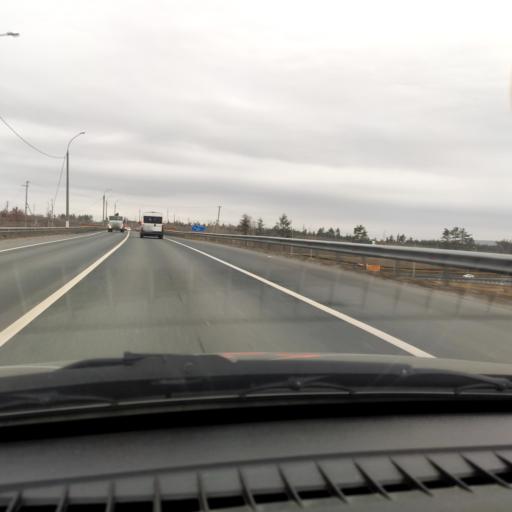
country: RU
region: Samara
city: Zhigulevsk
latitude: 53.5004
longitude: 49.5396
